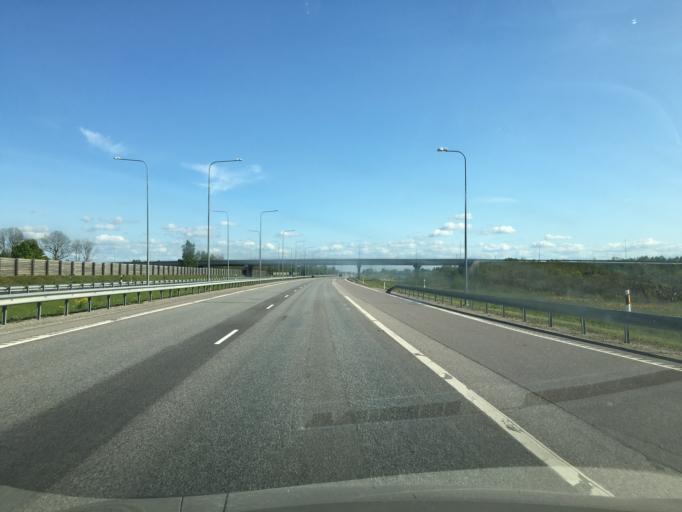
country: EE
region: Harju
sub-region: Rae vald
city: Vaida
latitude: 59.2921
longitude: 24.9637
